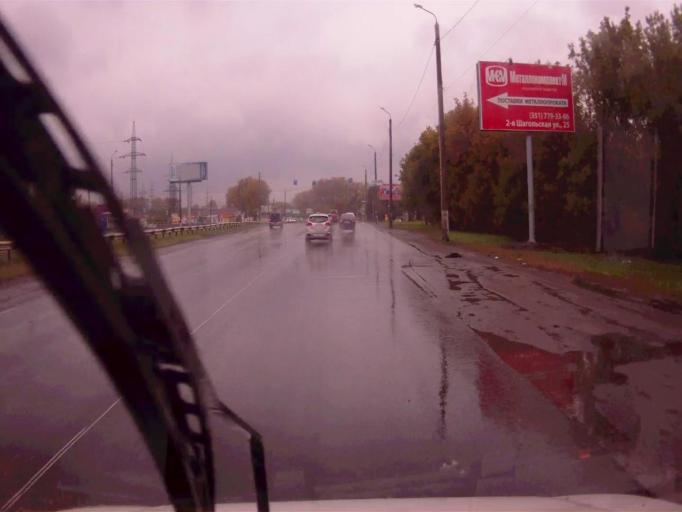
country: RU
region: Chelyabinsk
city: Dolgoderevenskoye
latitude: 55.2391
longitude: 61.3613
